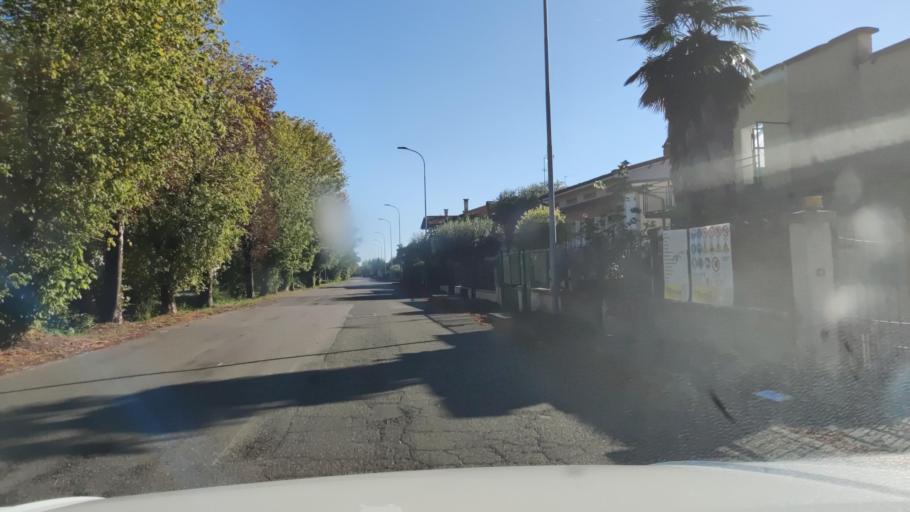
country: IT
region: Lombardy
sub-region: Provincia di Brescia
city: Orzinuovi
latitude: 45.4037
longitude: 9.9299
